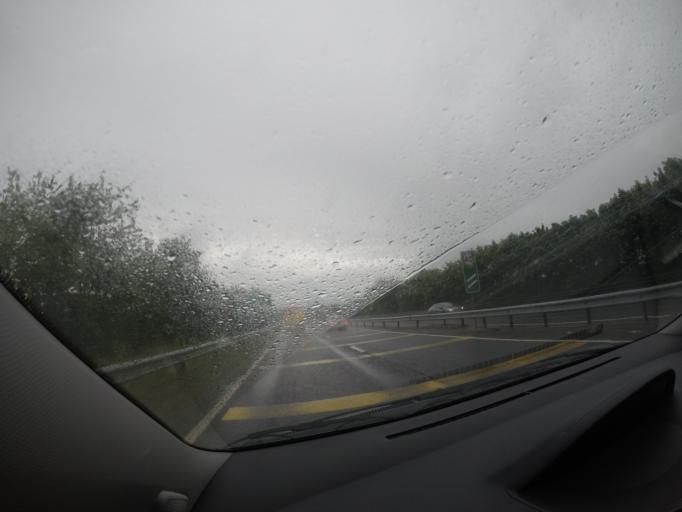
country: GB
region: Scotland
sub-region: Dundee City
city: Dundee
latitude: 56.4969
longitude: -2.9501
